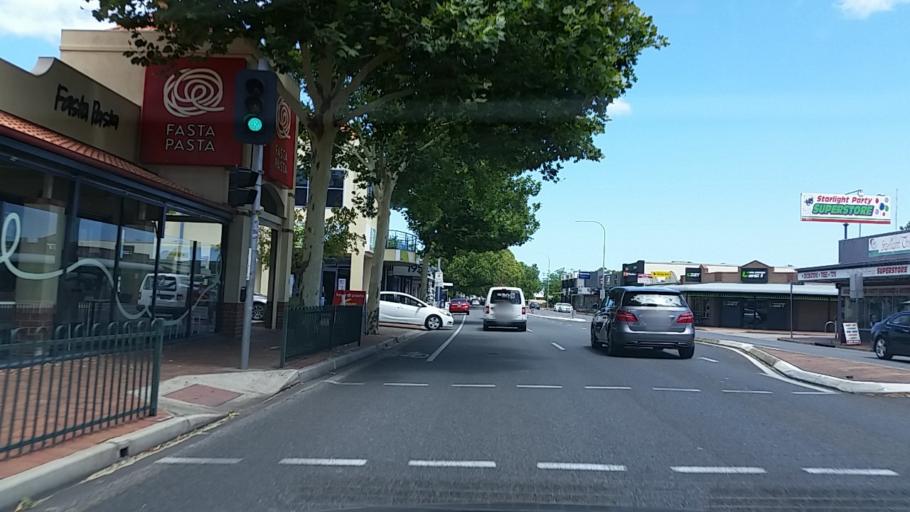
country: AU
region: South Australia
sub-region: City of West Torrens
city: Thebarton
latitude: -34.9243
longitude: 138.5595
